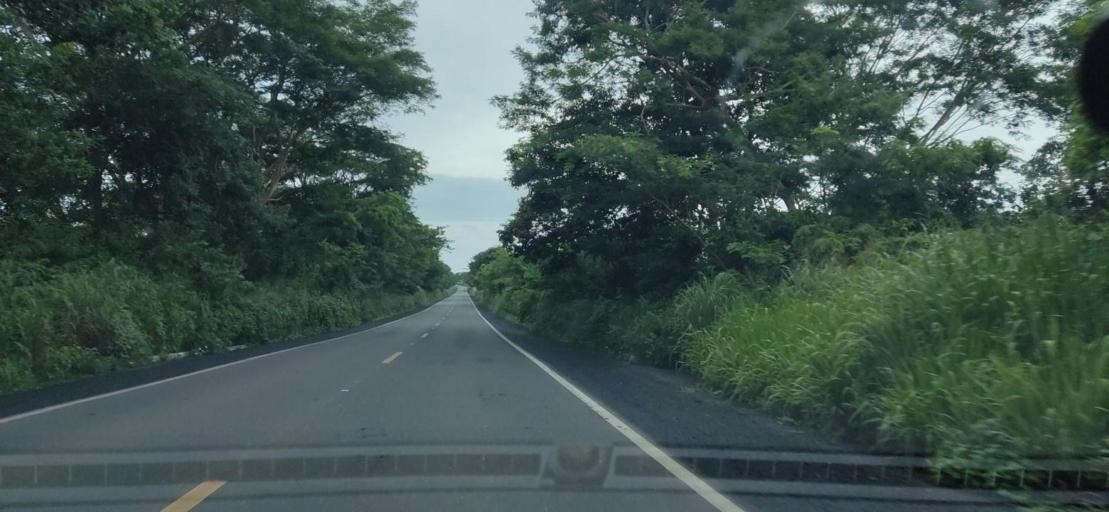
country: BR
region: Piaui
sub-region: Elesbao Veloso
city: Elesbao Veloso
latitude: -6.1996
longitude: -42.1115
